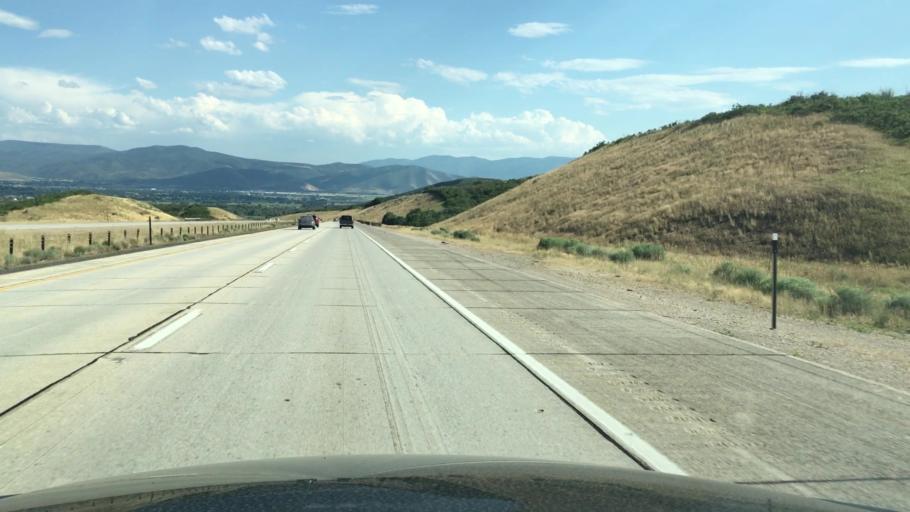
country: US
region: Utah
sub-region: Wasatch County
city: Heber
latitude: 40.5845
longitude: -111.4367
